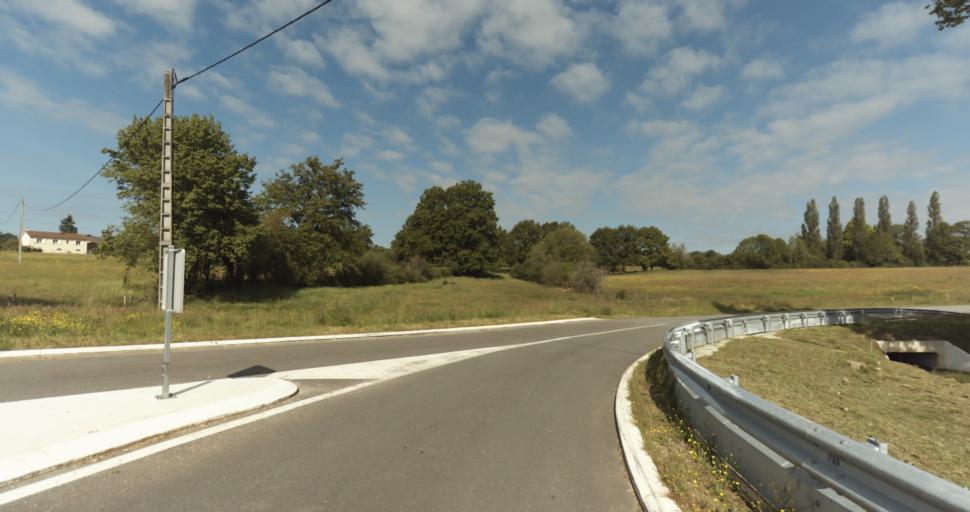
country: FR
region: Limousin
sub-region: Departement de la Haute-Vienne
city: Solignac
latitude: 45.7068
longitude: 1.2413
